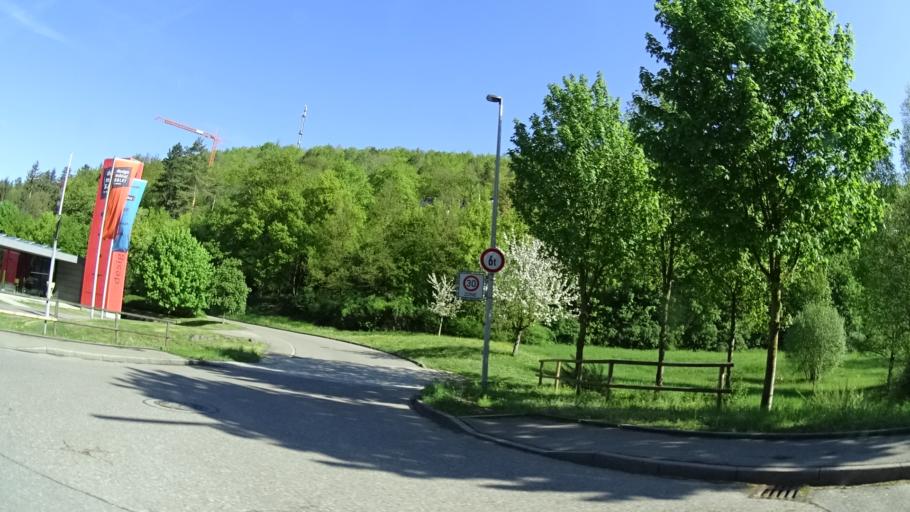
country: DE
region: Baden-Wuerttemberg
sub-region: Karlsruhe Region
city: Nagold
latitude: 48.5506
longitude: 8.7348
